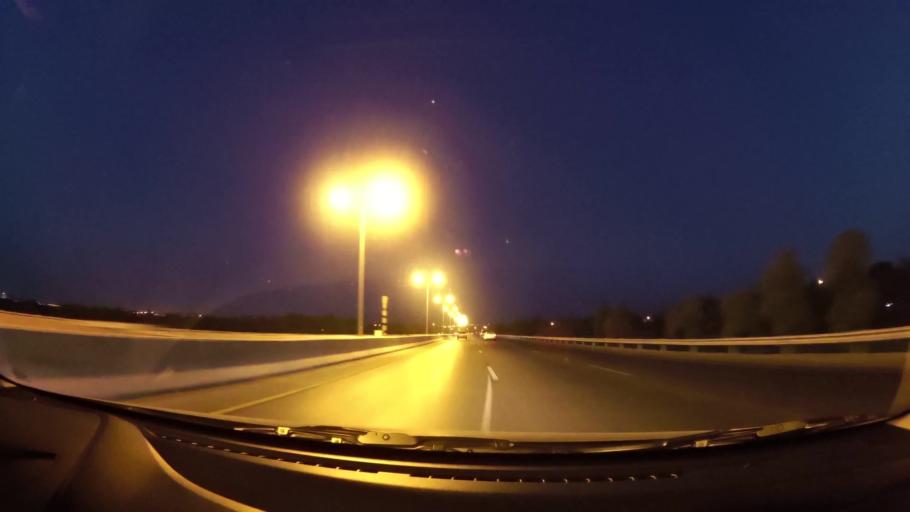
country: OM
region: Muhafazat Masqat
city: As Sib al Jadidah
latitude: 23.5896
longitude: 58.2533
